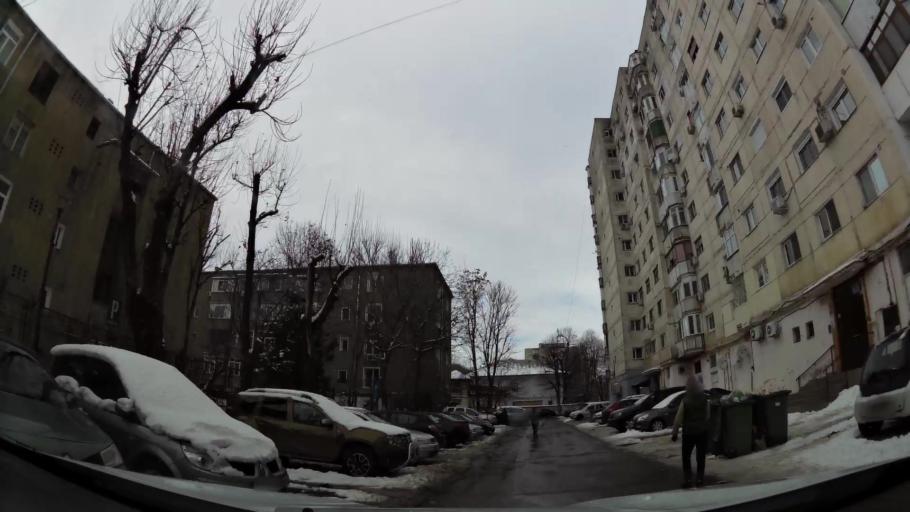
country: RO
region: Bucuresti
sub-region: Municipiul Bucuresti
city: Bucuresti
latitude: 44.3951
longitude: 26.1163
